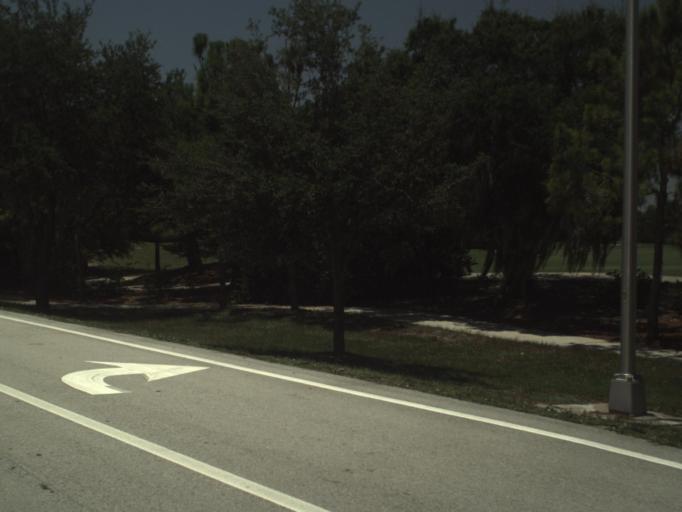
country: US
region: Florida
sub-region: Martin County
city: Palm City
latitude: 27.1695
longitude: -80.2987
